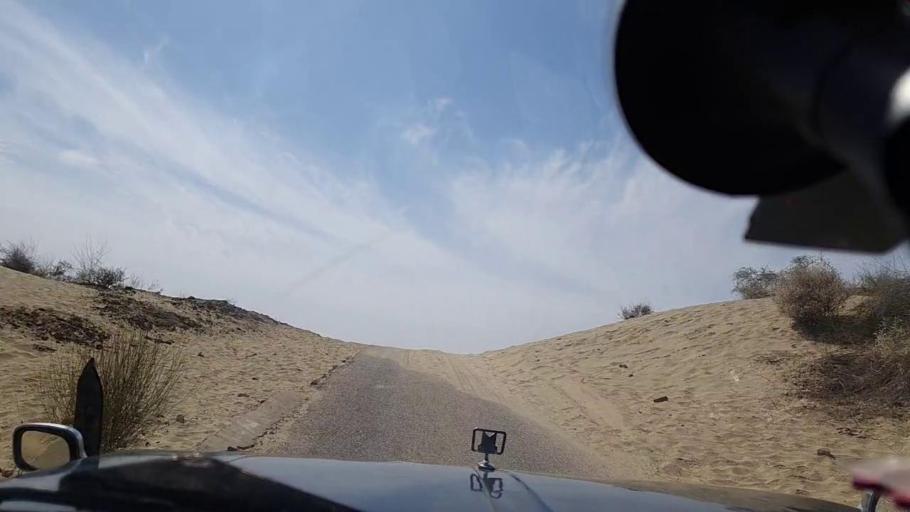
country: PK
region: Sindh
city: Diplo
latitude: 24.4142
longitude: 69.5853
